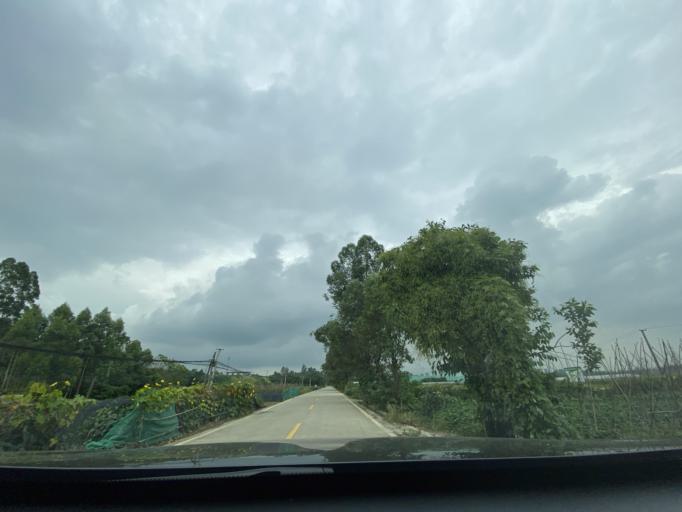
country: CN
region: Sichuan
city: Wujin
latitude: 30.3874
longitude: 103.9673
